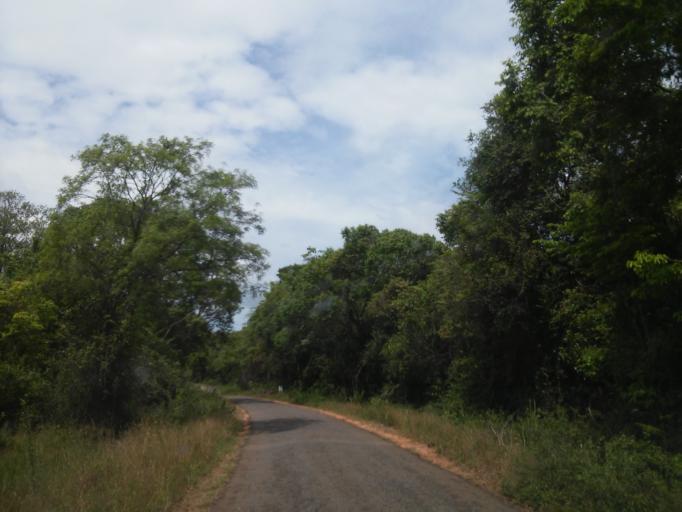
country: LK
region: Central
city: Sigiriya
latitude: 8.0938
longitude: 80.6811
